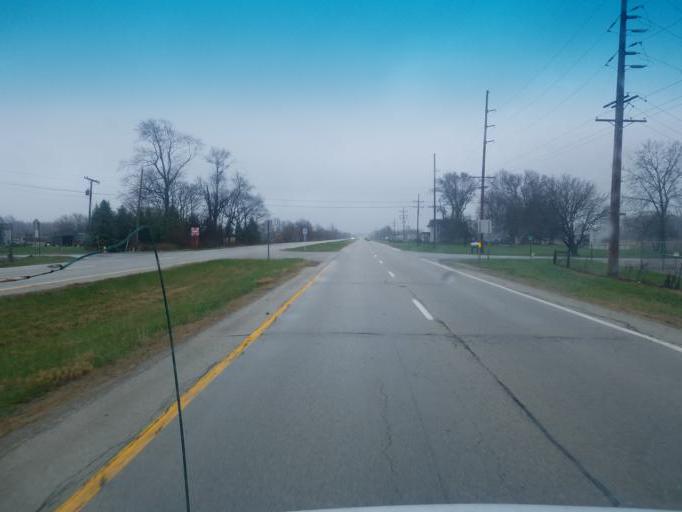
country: US
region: Ohio
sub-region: Wood County
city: North Baltimore
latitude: 41.2689
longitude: -83.6503
